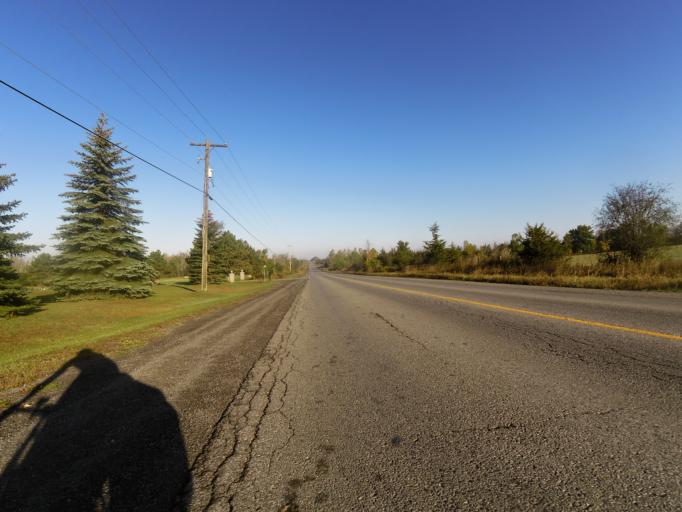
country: CA
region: Ontario
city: Belleville
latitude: 44.0562
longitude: -77.3924
